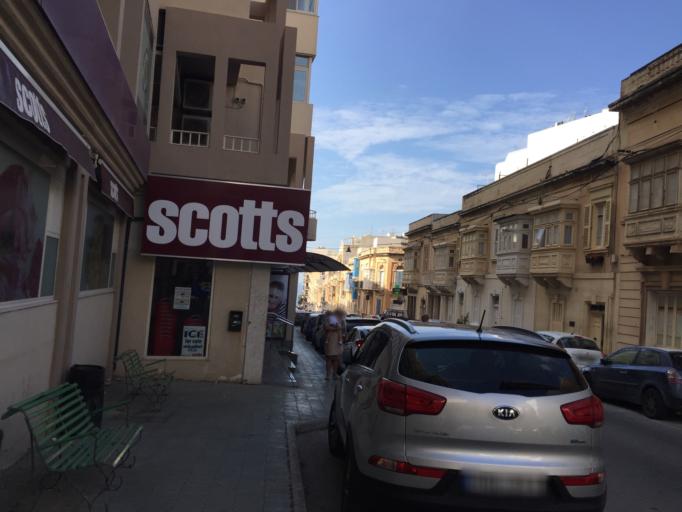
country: MT
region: Tas-Sliema
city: Sliema
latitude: 35.9123
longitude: 14.5046
